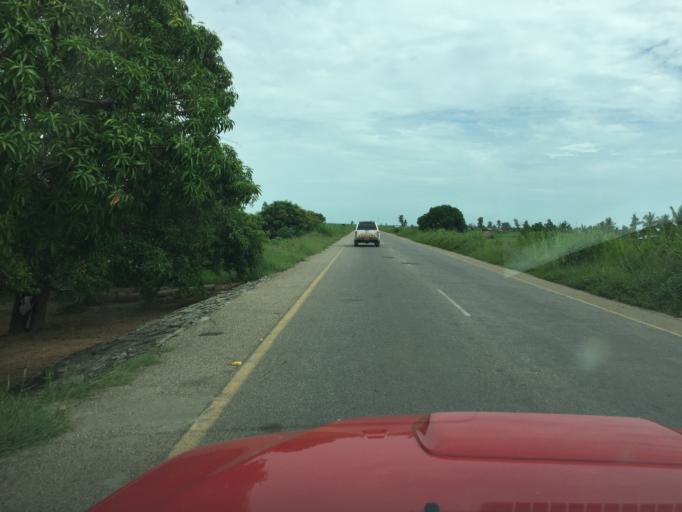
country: MZ
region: Zambezia
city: Quelimane
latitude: -17.7135
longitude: 36.8930
